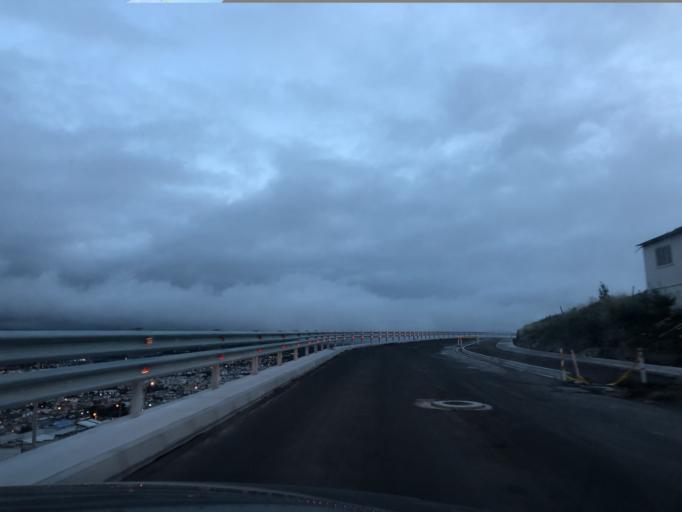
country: EC
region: Imbabura
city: Ibarra
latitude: 0.3721
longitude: -78.1287
